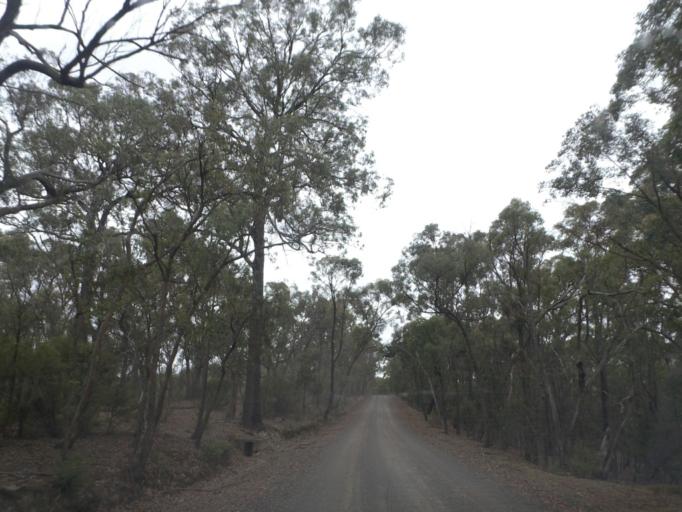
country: AU
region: Victoria
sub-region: Yarra Ranges
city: Yarra Glen
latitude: -37.6825
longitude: 145.3237
